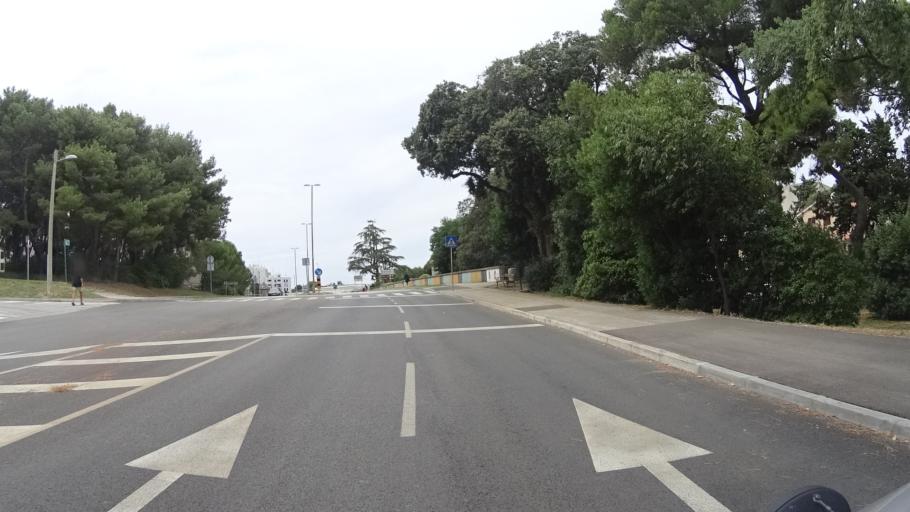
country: HR
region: Istarska
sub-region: Grad Pula
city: Pula
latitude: 44.8556
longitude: 13.8368
